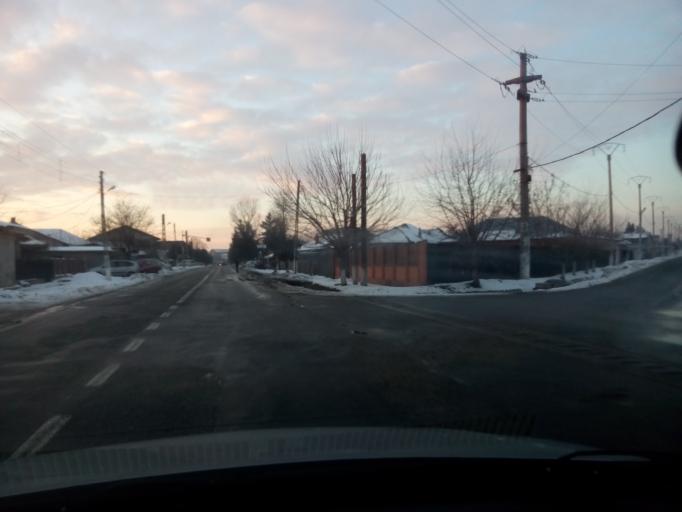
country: RO
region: Calarasi
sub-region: Comuna Budesti
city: Budesti
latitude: 44.2332
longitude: 26.4700
